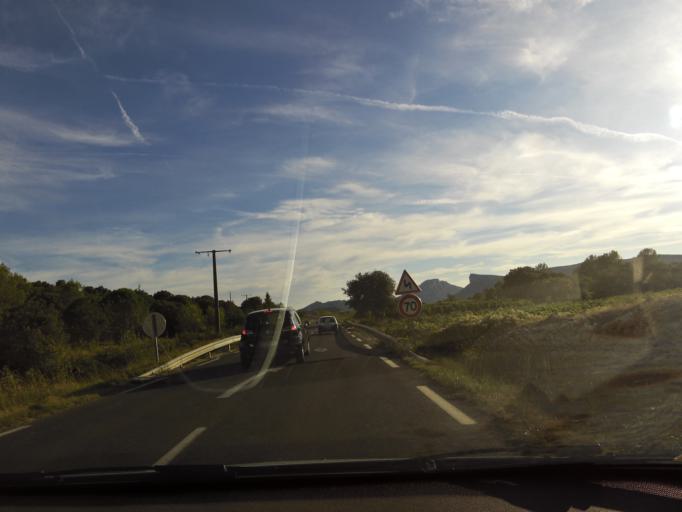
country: FR
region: Languedoc-Roussillon
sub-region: Departement de l'Herault
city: Claret
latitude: 43.8185
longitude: 3.8934
